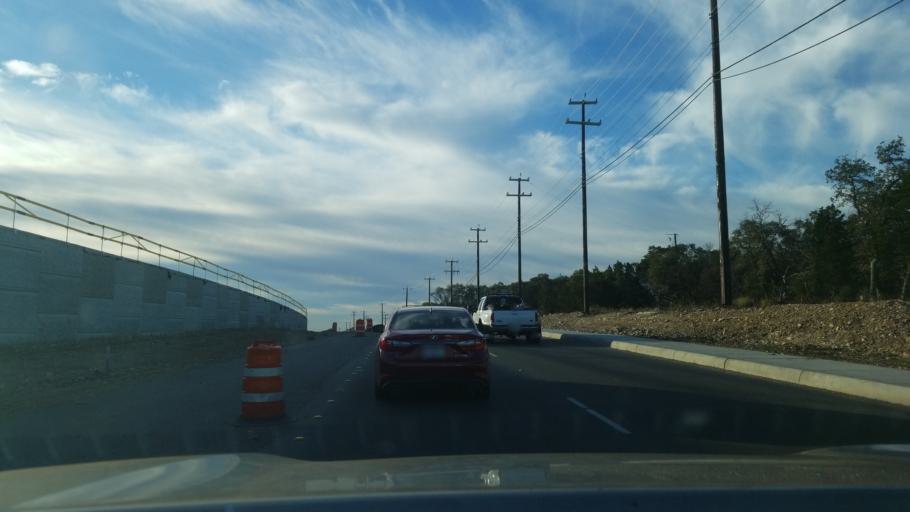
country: US
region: Texas
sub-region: Bexar County
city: Timberwood Park
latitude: 29.6601
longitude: -98.4509
